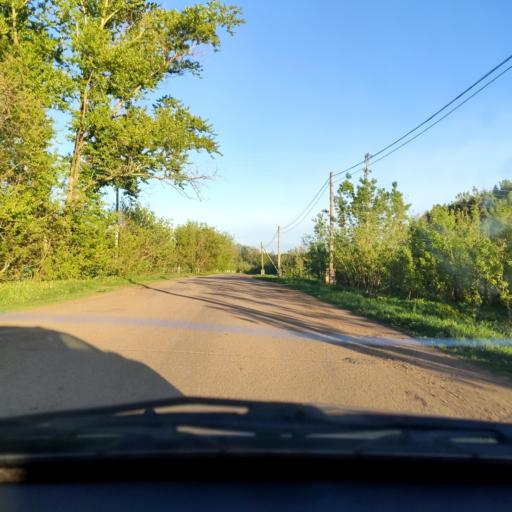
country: RU
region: Bashkortostan
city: Yazykovo
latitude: 55.0428
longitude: 56.1871
